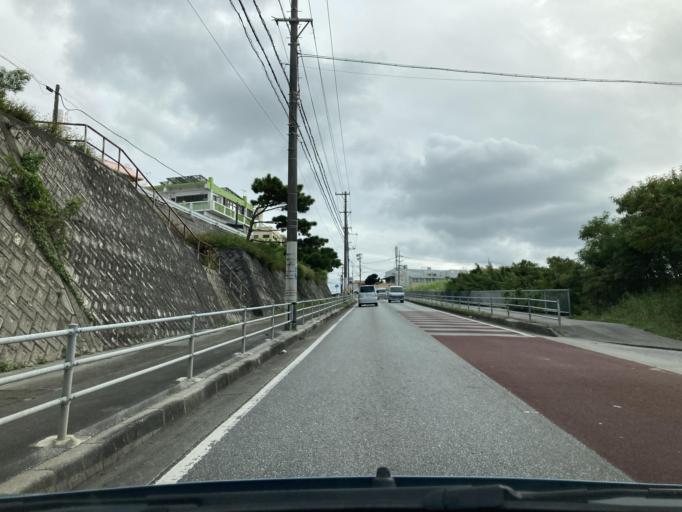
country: JP
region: Okinawa
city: Tomigusuku
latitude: 26.1628
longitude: 127.6796
